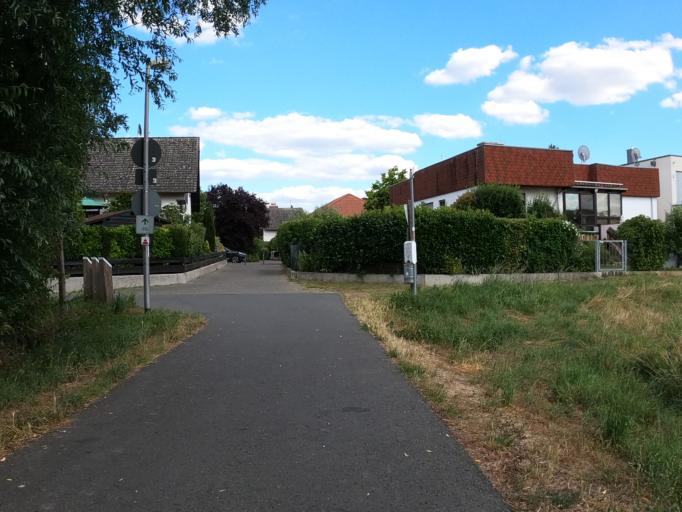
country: DE
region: Hesse
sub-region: Regierungsbezirk Darmstadt
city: Gross-Gerau
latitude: 49.9072
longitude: 8.4715
